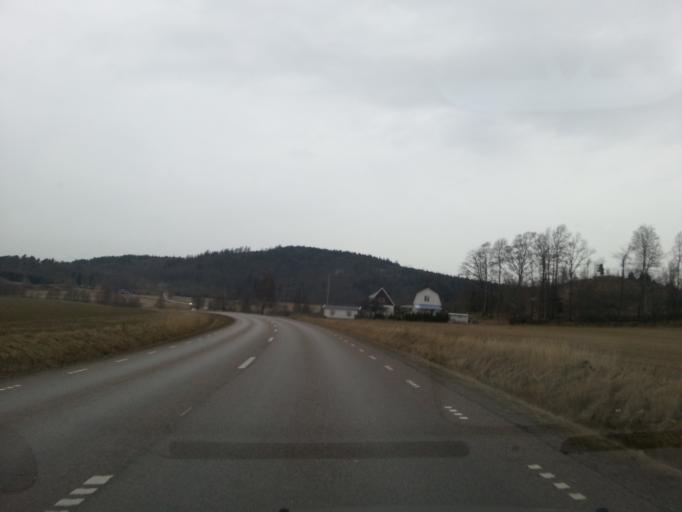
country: SE
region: Vaestra Goetaland
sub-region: Lilla Edets Kommun
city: Lilla Edet
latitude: 58.1399
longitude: 12.0985
